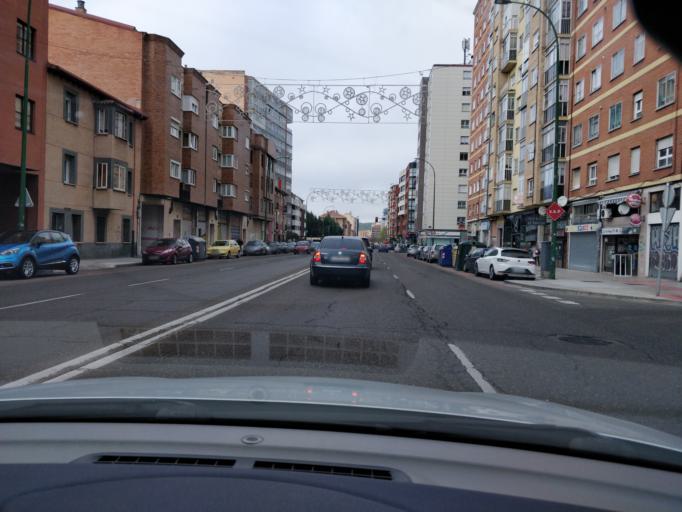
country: ES
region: Castille and Leon
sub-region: Provincia de Burgos
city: Burgos
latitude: 42.3473
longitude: -3.6671
